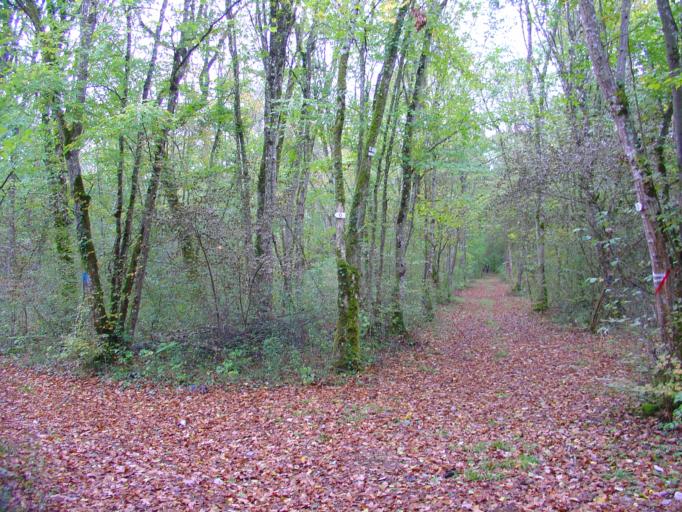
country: FR
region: Lorraine
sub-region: Departement de Meurthe-et-Moselle
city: Colombey-les-Belles
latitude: 48.5924
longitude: 5.9084
